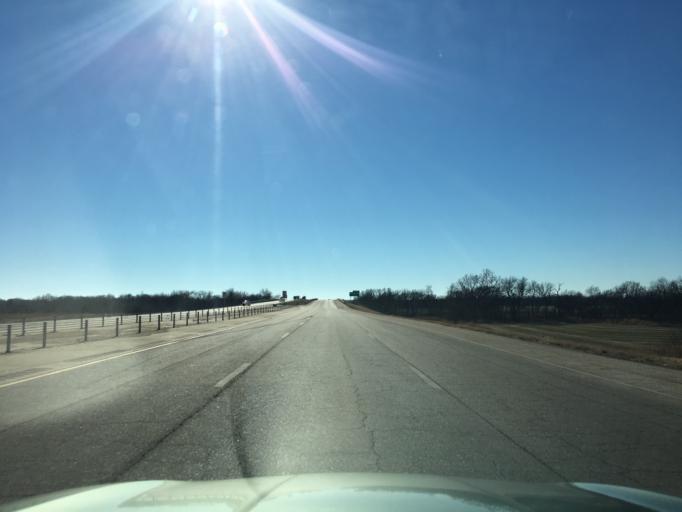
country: US
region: Oklahoma
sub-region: Kay County
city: Blackwell
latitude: 36.9372
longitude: -97.3474
